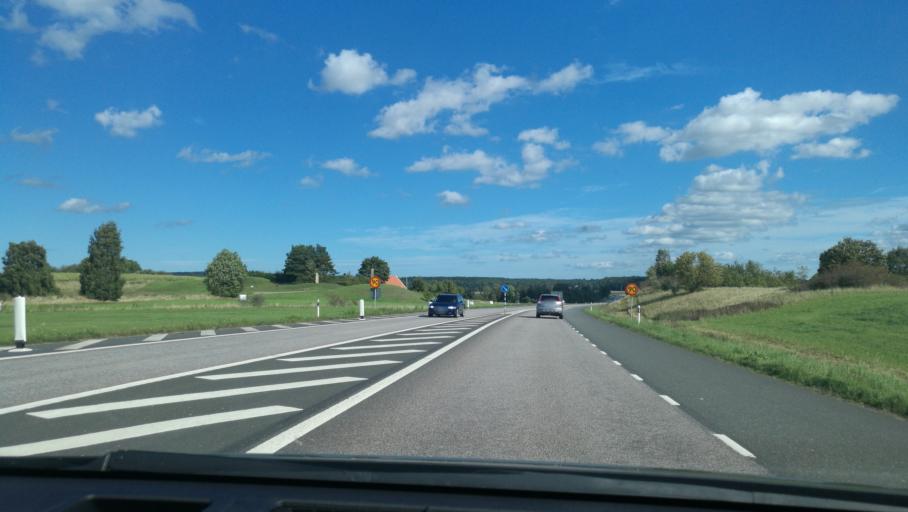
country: SE
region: Vaestra Goetaland
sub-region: Gotene Kommun
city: Kallby
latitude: 58.5052
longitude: 13.3134
